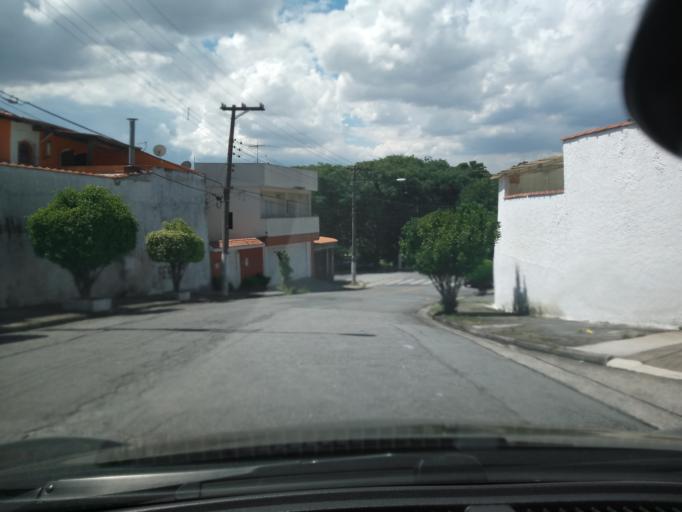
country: BR
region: Sao Paulo
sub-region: Sao Bernardo Do Campo
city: Sao Bernardo do Campo
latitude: -23.7035
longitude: -46.5744
